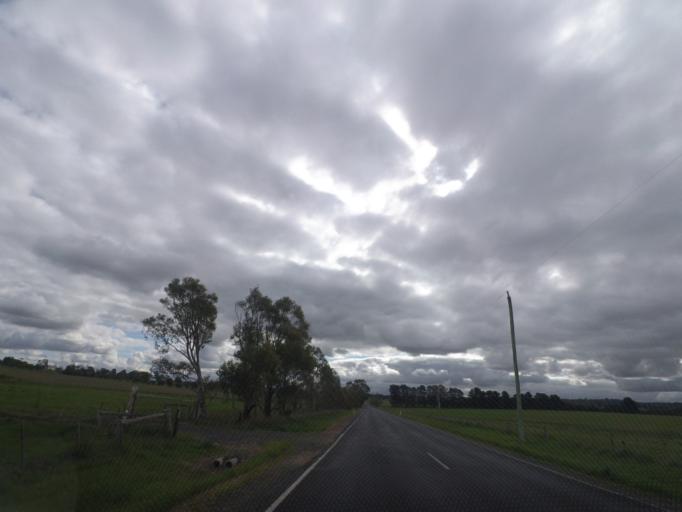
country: AU
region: Victoria
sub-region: Whittlesea
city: Whittlesea
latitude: -37.5257
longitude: 145.0852
